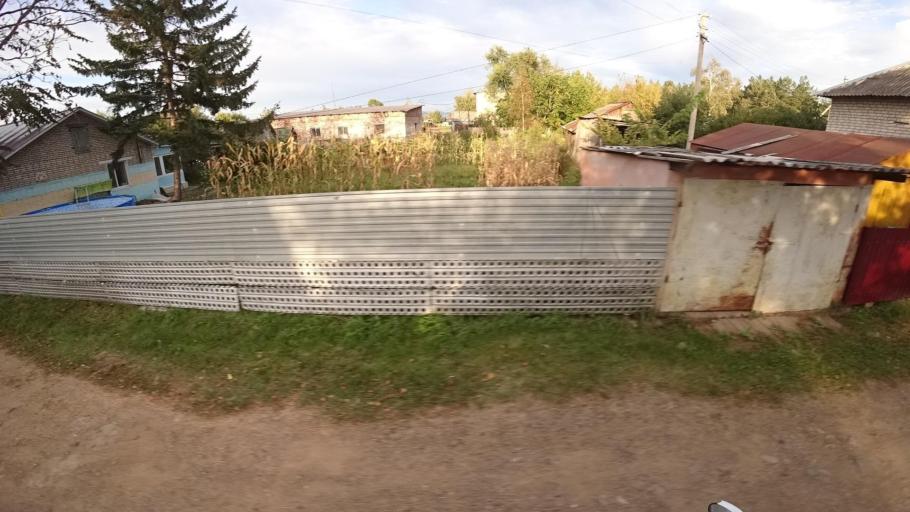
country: RU
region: Primorskiy
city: Yakovlevka
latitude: 44.4267
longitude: 133.4720
